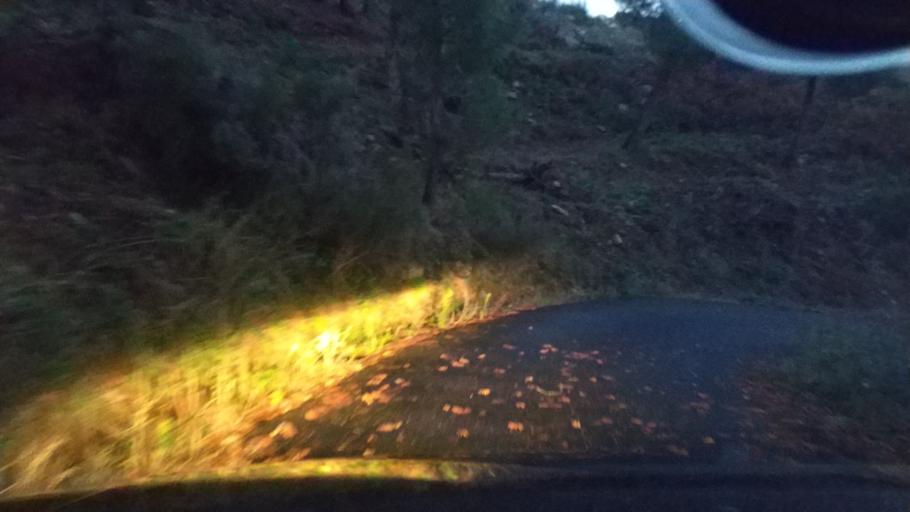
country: PT
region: Vila Real
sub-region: Santa Marta de Penaguiao
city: Santa Marta de Penaguiao
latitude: 41.2559
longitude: -7.7750
